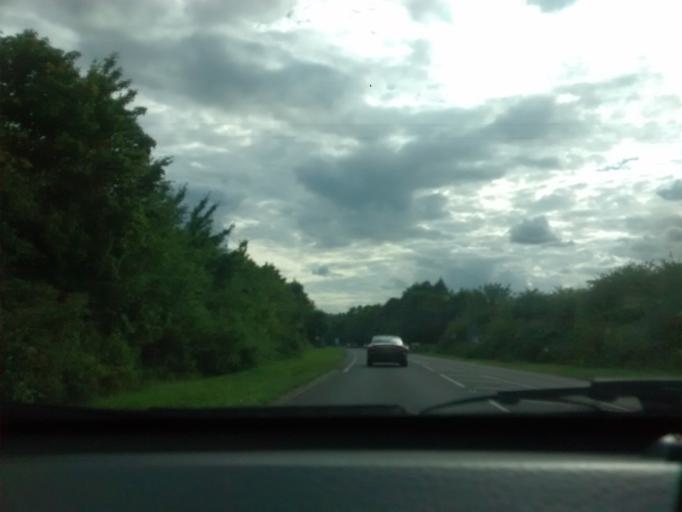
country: GB
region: England
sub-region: Norfolk
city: Downham Market
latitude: 52.5916
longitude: 0.3904
